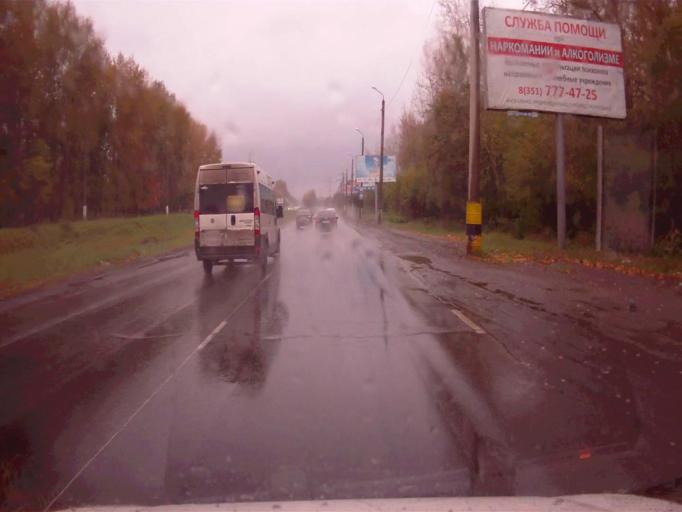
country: RU
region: Chelyabinsk
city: Dolgoderevenskoye
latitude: 55.2438
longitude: 61.3602
